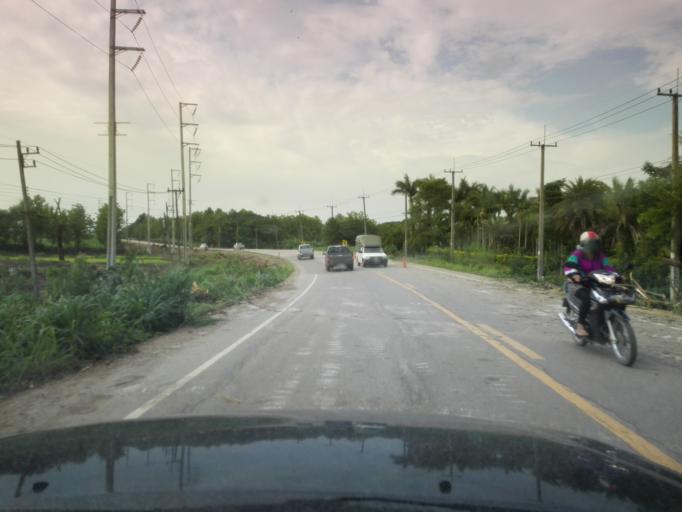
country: TH
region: Tak
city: Mae Sot
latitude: 16.8059
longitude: 98.5992
